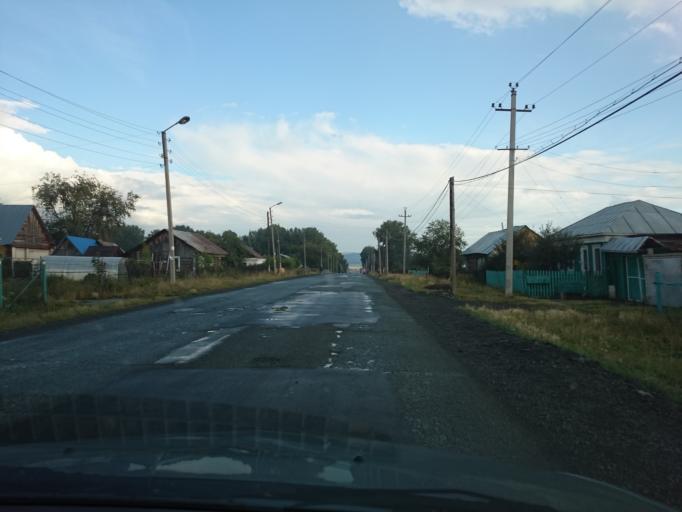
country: RU
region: Bashkortostan
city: Beloretsk
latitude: 53.9659
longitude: 58.3557
